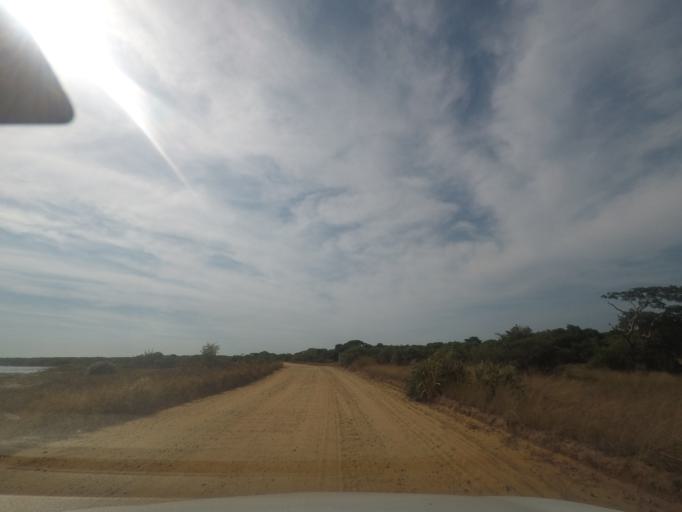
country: BR
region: Rio de Janeiro
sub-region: Marica
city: Marica
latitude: -22.9563
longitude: -42.8844
